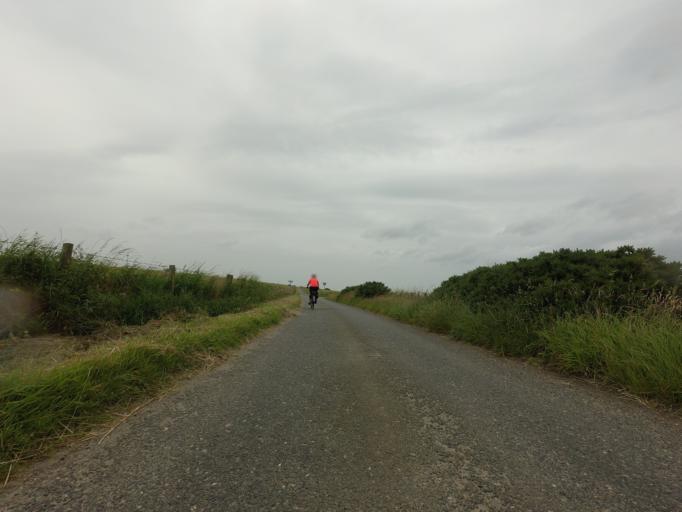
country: GB
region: Scotland
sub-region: Moray
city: Cullen
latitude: 57.6639
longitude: -2.7610
